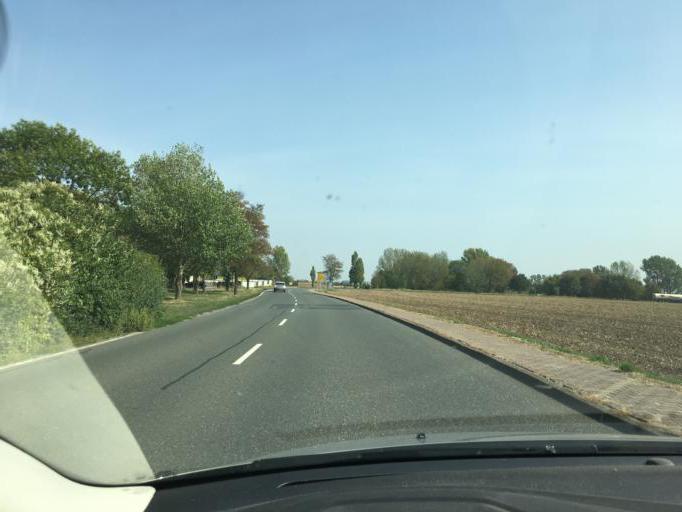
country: DE
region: Saxony-Anhalt
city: Barby
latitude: 51.9917
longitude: 11.8391
